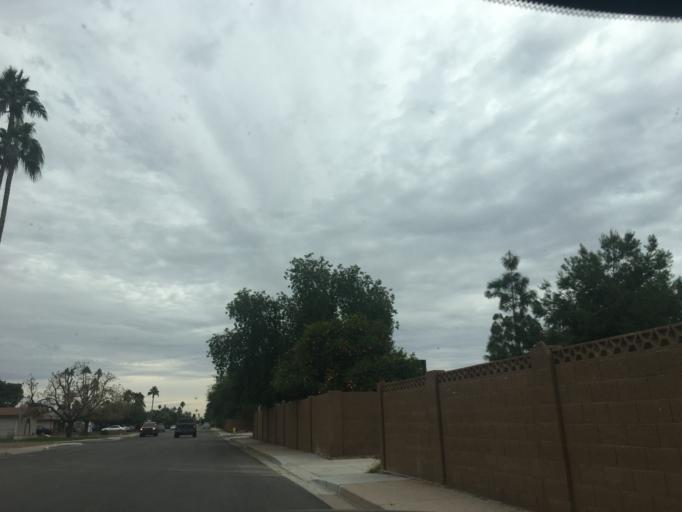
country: US
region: Arizona
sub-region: Maricopa County
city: Tempe
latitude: 33.3823
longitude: -111.9007
